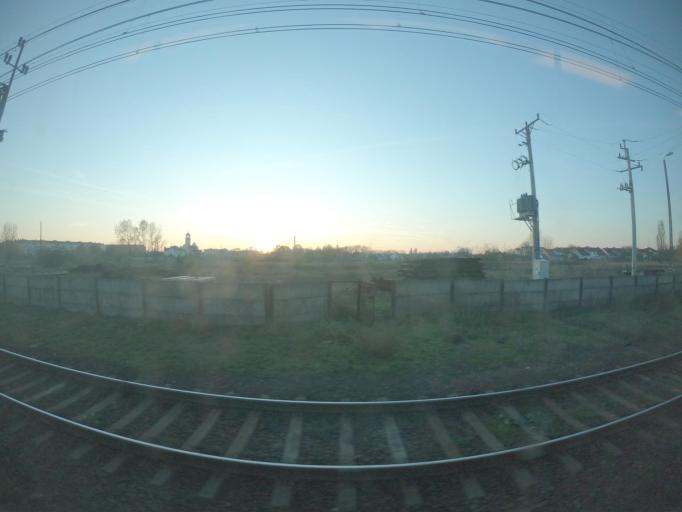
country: PL
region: Lubusz
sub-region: Powiat gorzowski
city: Kostrzyn nad Odra
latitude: 52.5998
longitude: 14.6474
